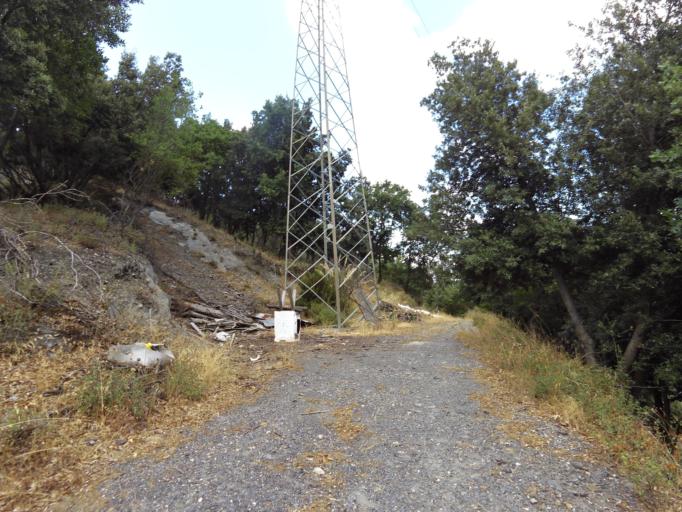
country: IT
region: Calabria
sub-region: Provincia di Reggio Calabria
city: Pazzano
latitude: 38.4704
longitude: 16.4322
